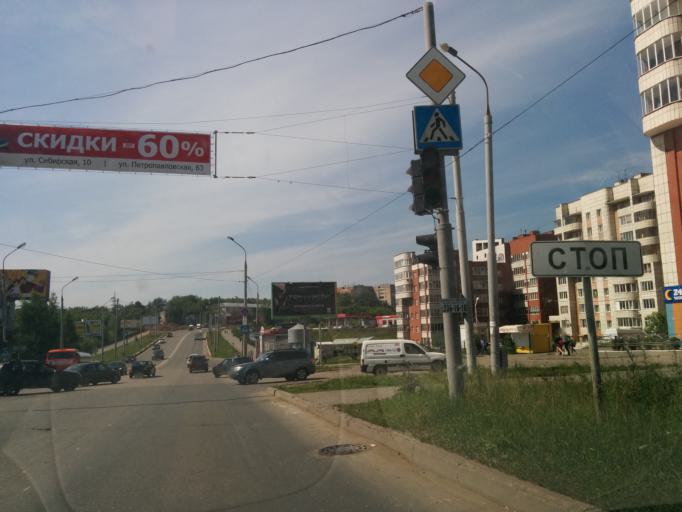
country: RU
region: Perm
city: Perm
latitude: 58.0075
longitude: 56.3006
